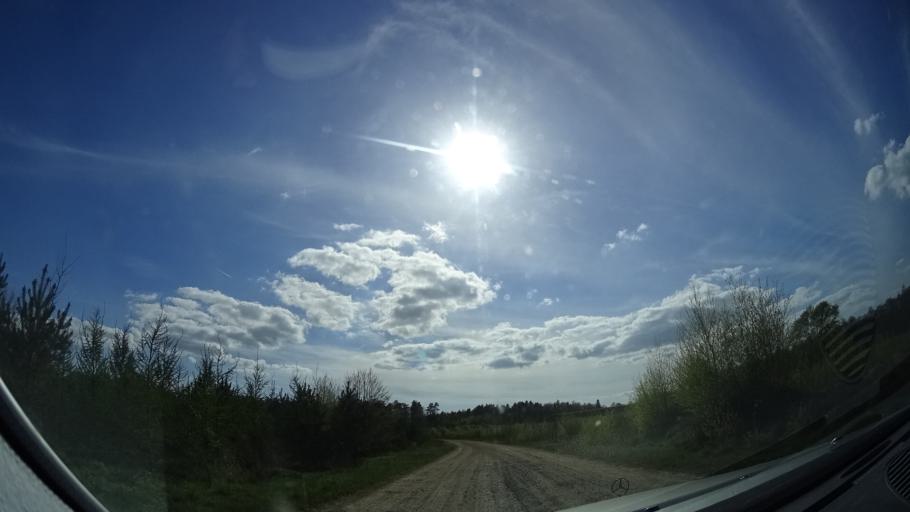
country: SE
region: Skane
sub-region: Hassleholms Kommun
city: Tormestorp
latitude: 56.1040
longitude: 13.6738
